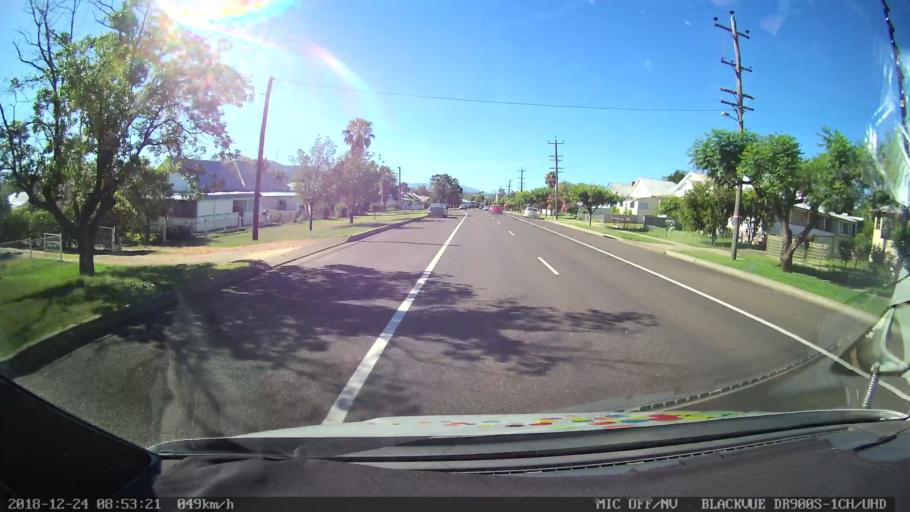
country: AU
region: New South Wales
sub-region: Liverpool Plains
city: Quirindi
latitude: -31.4977
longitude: 150.6812
